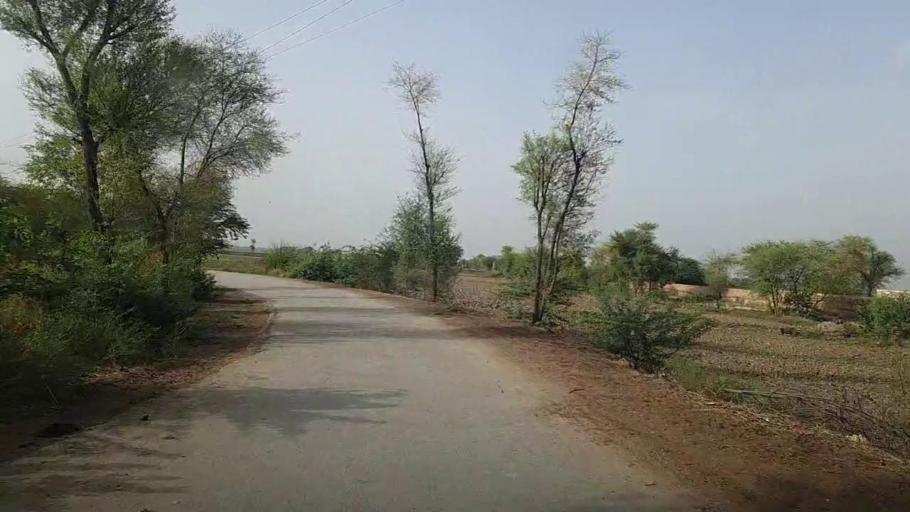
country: PK
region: Sindh
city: Khairpur Nathan Shah
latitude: 27.1116
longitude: 67.7884
